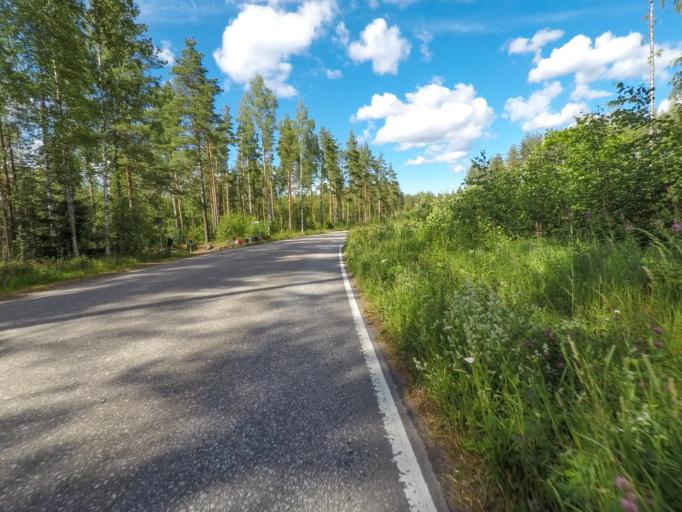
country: FI
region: South Karelia
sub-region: Lappeenranta
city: Joutseno
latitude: 61.1051
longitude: 28.3713
